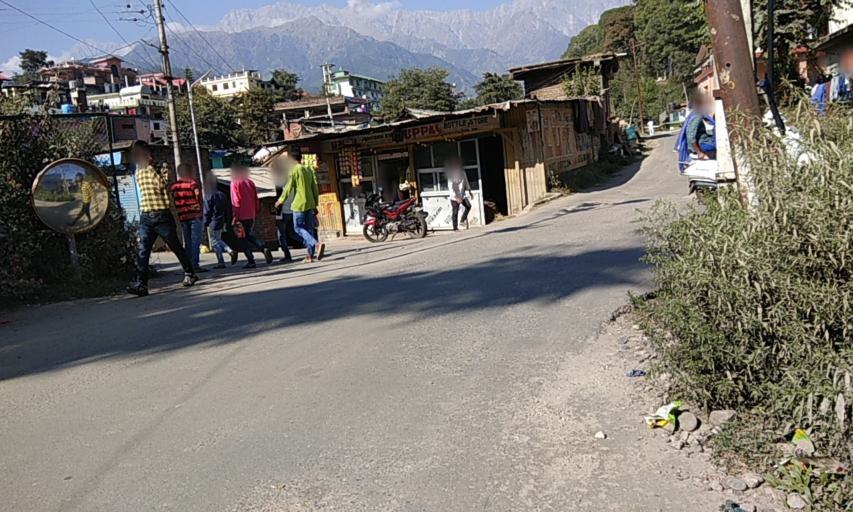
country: IN
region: Himachal Pradesh
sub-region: Kangra
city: Palampur
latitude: 32.1097
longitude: 76.5343
